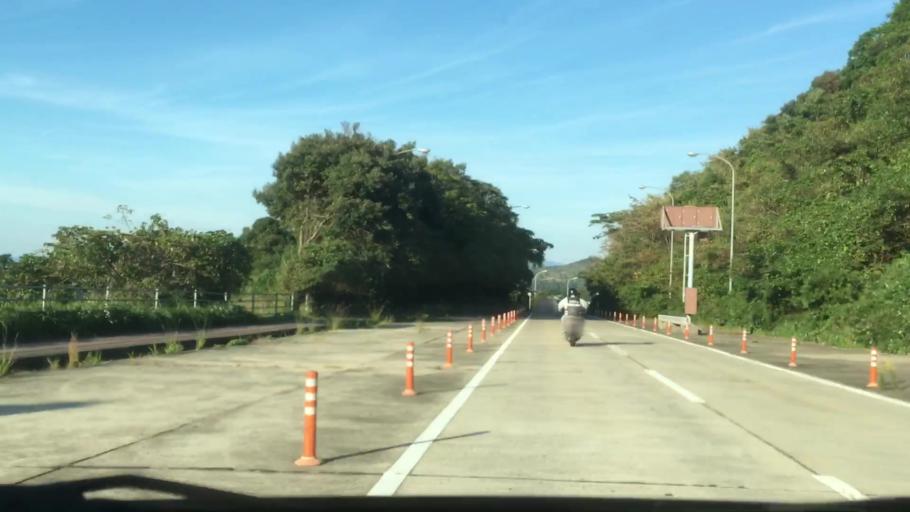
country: JP
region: Nagasaki
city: Sasebo
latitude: 33.0384
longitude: 129.6494
